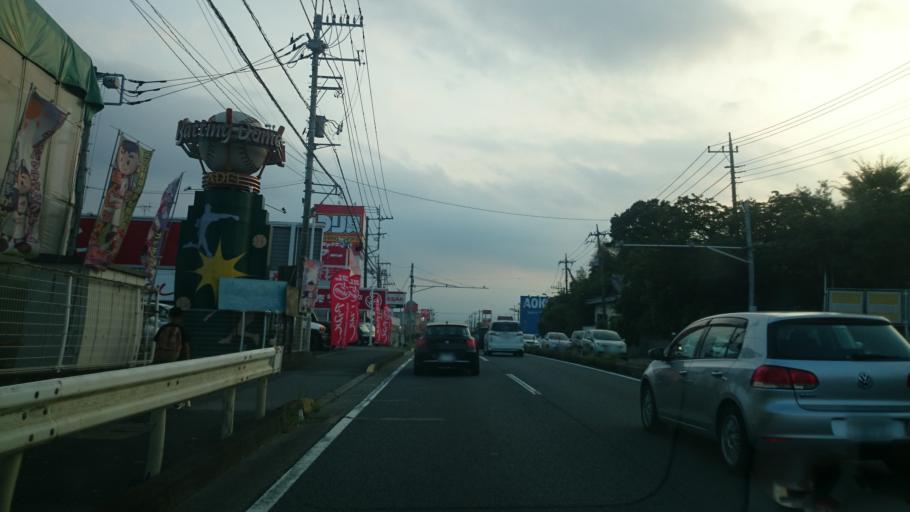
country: JP
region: Saitama
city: Iwatsuki
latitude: 35.9462
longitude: 139.7131
